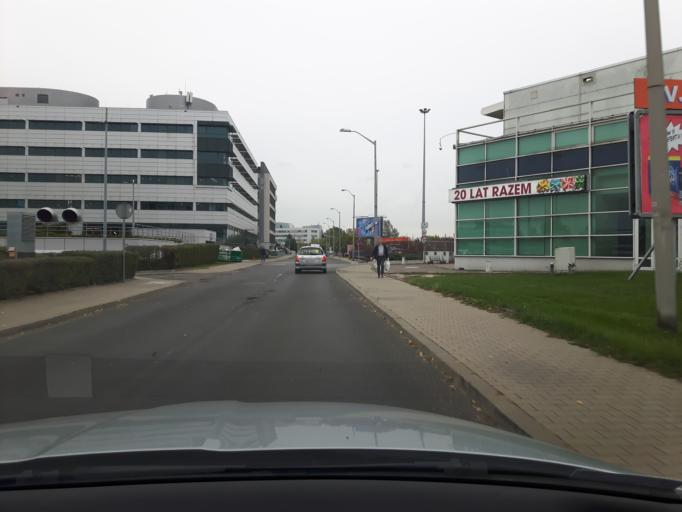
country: PL
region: Masovian Voivodeship
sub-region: Warszawa
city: Wlochy
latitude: 52.1995
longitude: 20.9356
